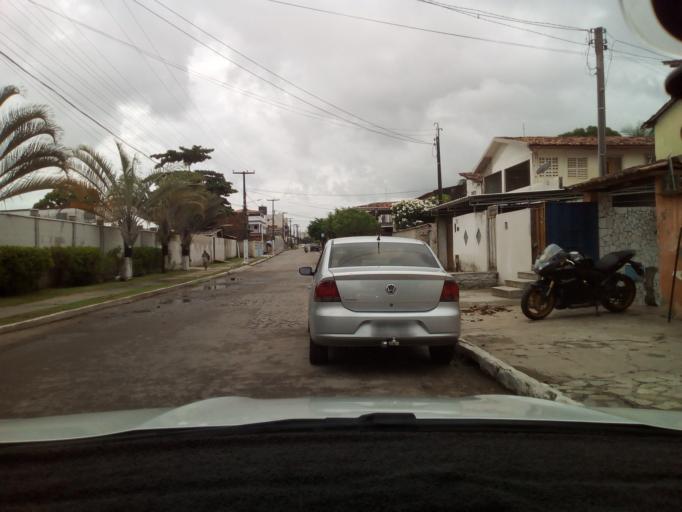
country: BR
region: Paraiba
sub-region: Joao Pessoa
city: Joao Pessoa
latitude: -7.1715
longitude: -34.8891
